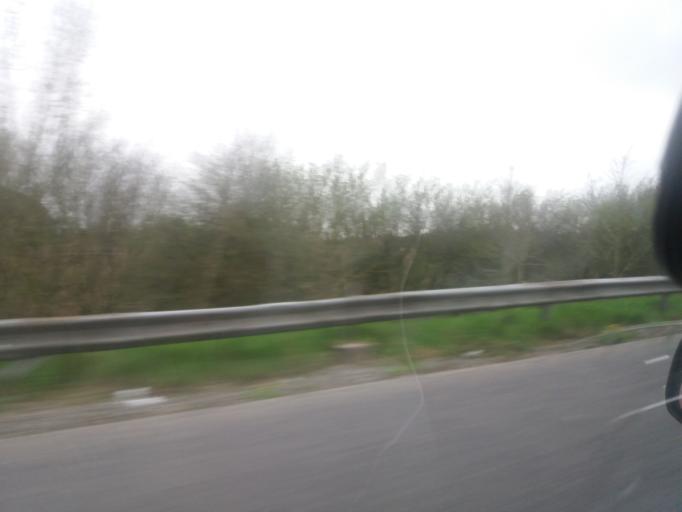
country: IE
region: Munster
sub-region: County Limerick
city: Rathkeale
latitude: 52.5153
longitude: -8.9639
